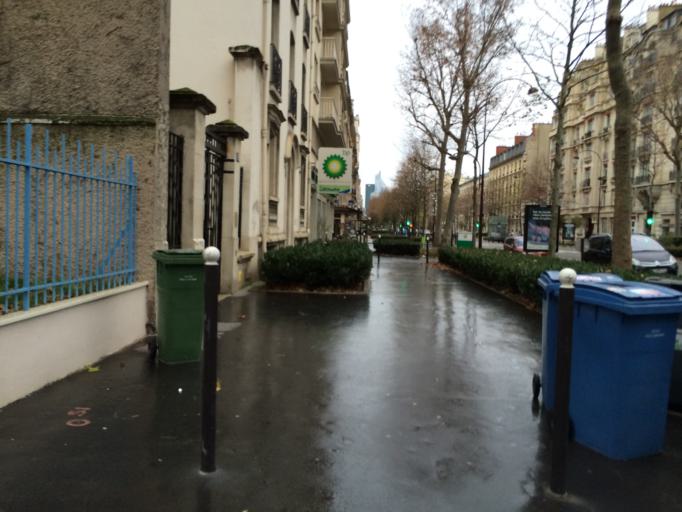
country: FR
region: Ile-de-France
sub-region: Departement des Hauts-de-Seine
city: Neuilly-sur-Seine
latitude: 48.8817
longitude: 2.2809
